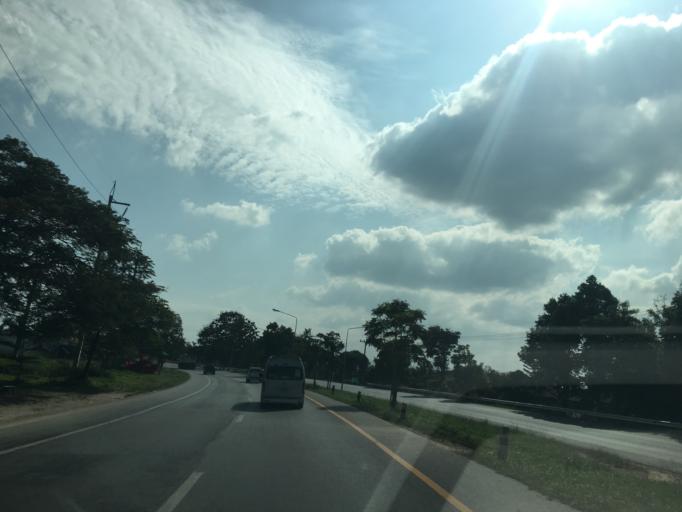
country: TH
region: Chiang Rai
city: Mae Lao
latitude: 19.7066
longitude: 99.7194
